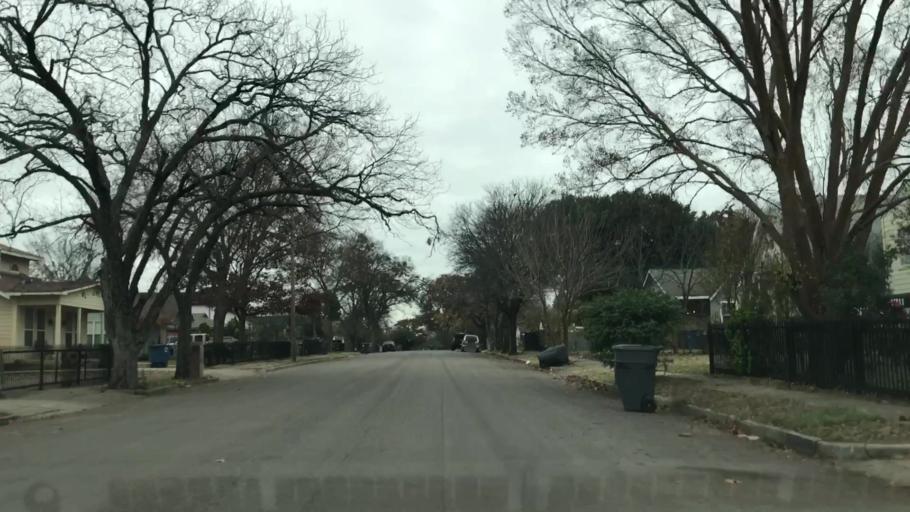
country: US
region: Texas
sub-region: Dallas County
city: Cockrell Hill
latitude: 32.7329
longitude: -96.8492
